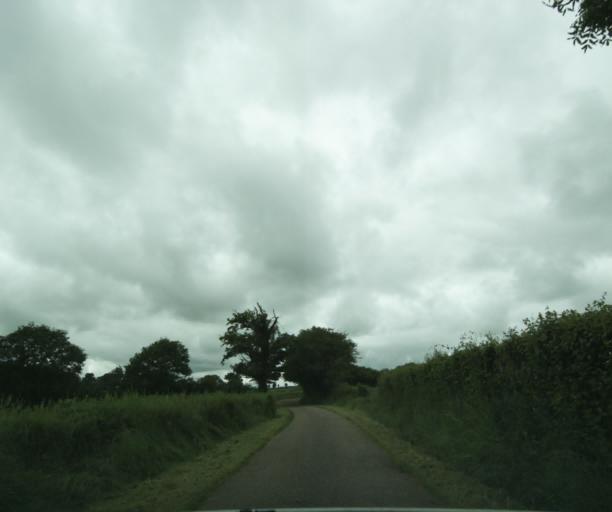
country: FR
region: Bourgogne
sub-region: Departement de Saone-et-Loire
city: Charolles
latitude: 46.4629
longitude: 4.2862
